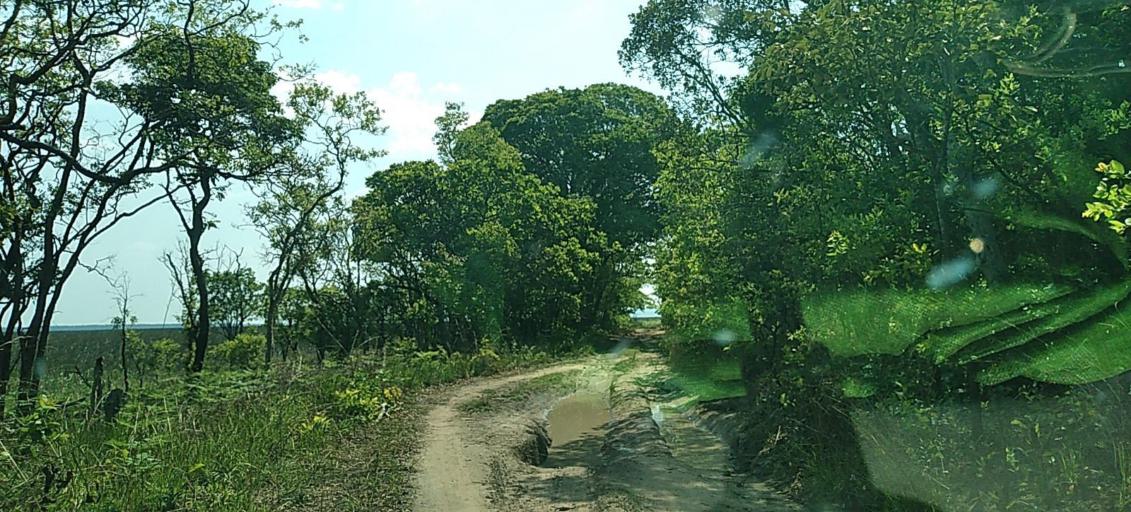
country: ZM
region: North-Western
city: Mwinilunga
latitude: -11.2733
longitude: 24.9865
